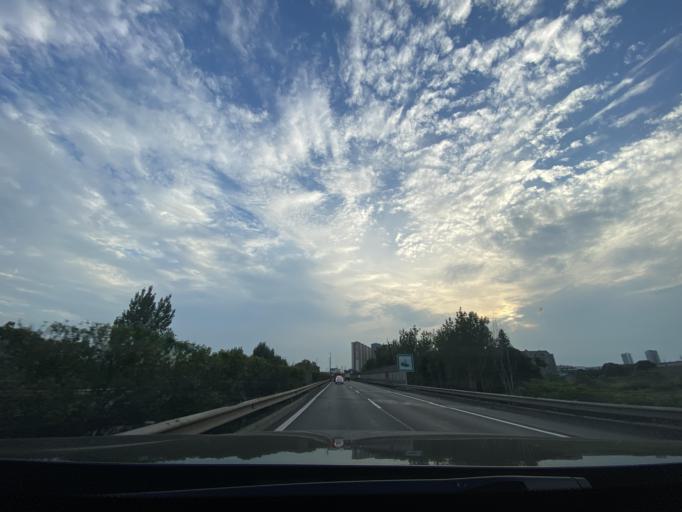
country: CN
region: Sichuan
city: Deyang
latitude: 31.0824
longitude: 104.3930
